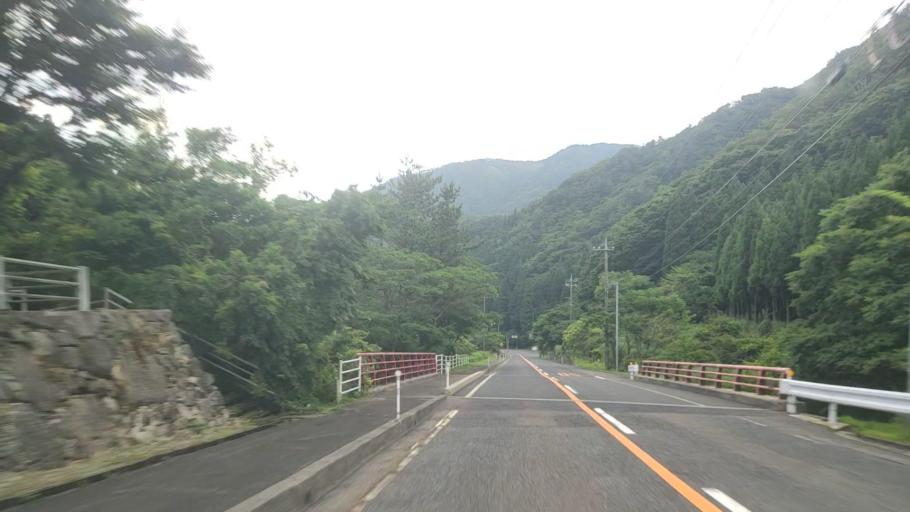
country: JP
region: Tottori
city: Kurayoshi
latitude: 35.3162
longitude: 133.8997
